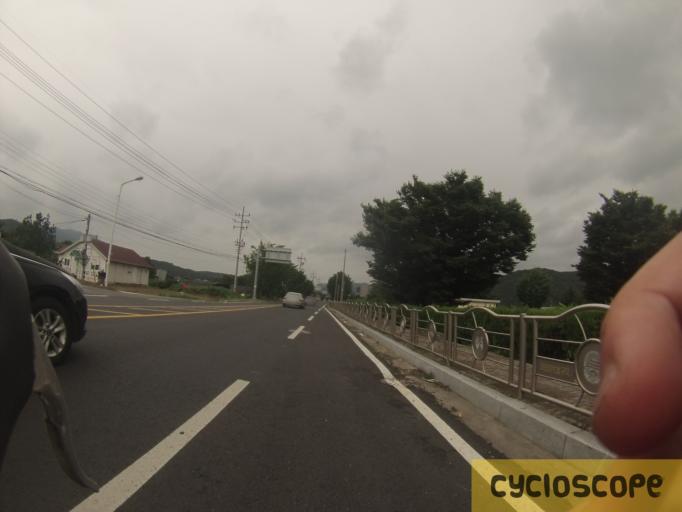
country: KR
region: Chungcheongnam-do
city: Hongsung
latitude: 36.4776
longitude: 126.7374
